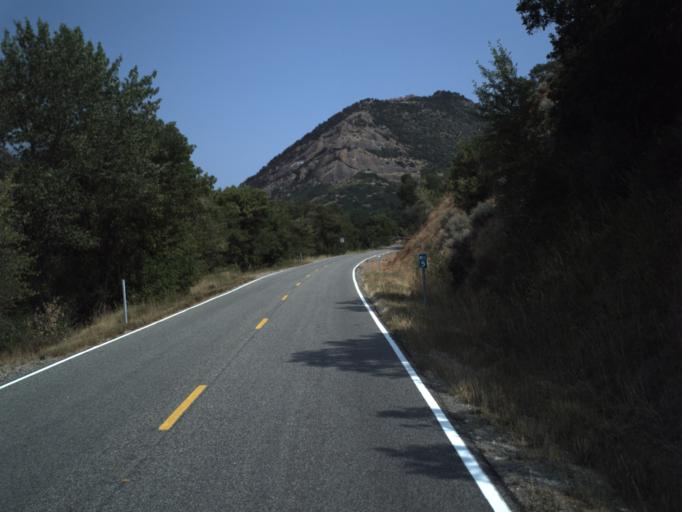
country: US
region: Utah
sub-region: Summit County
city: Summit Park
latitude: 40.8050
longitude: -111.6781
